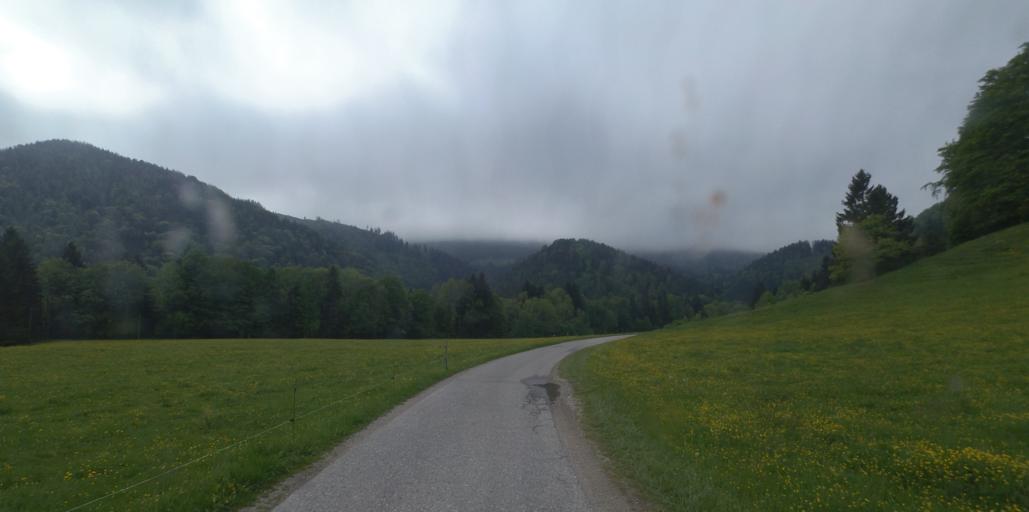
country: DE
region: Bavaria
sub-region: Upper Bavaria
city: Bernau am Chiemsee
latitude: 47.7856
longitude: 12.3617
